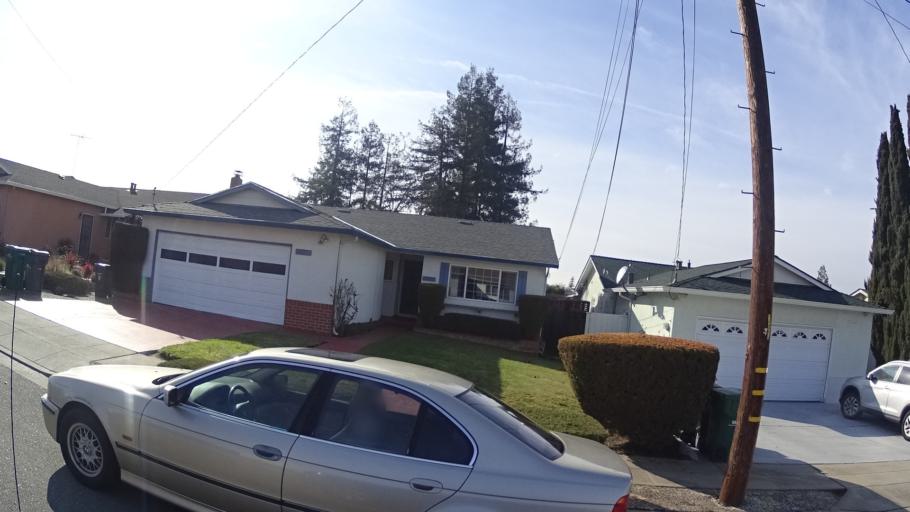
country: US
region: California
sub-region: Alameda County
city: Fairview
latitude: 37.6874
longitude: -122.0512
